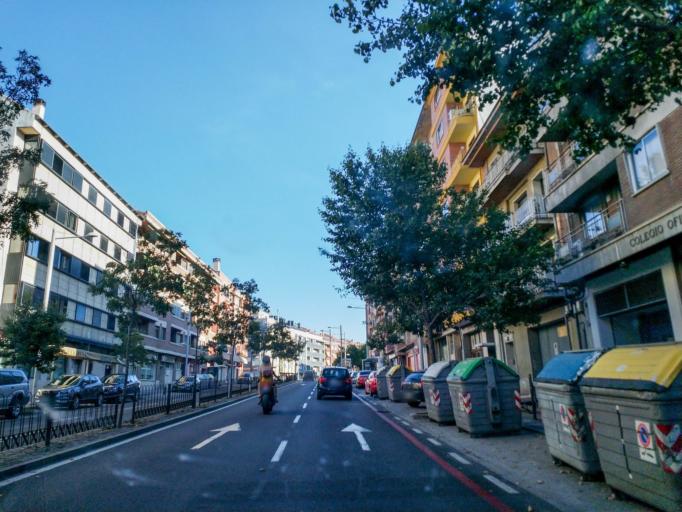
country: ES
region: Castille and Leon
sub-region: Provincia de Segovia
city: Segovia
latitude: 40.9382
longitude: -4.1148
